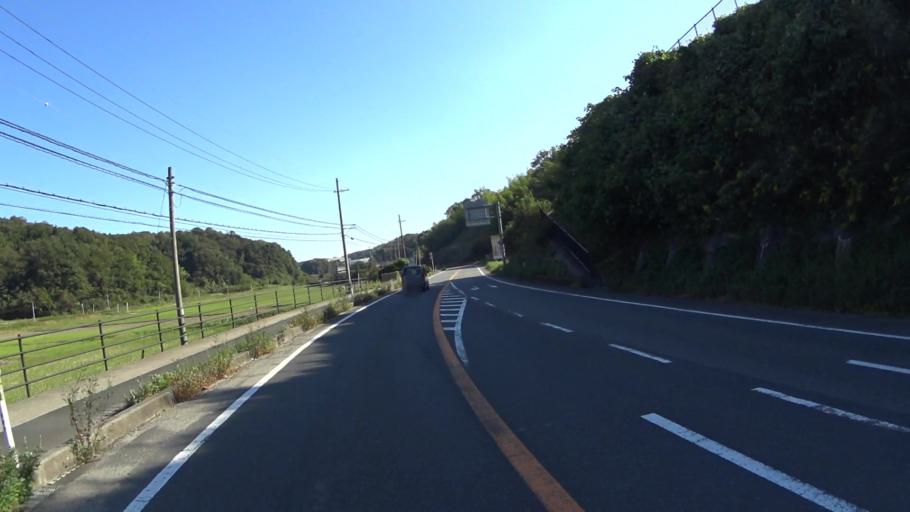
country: JP
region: Kyoto
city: Miyazu
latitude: 35.6440
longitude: 135.0508
